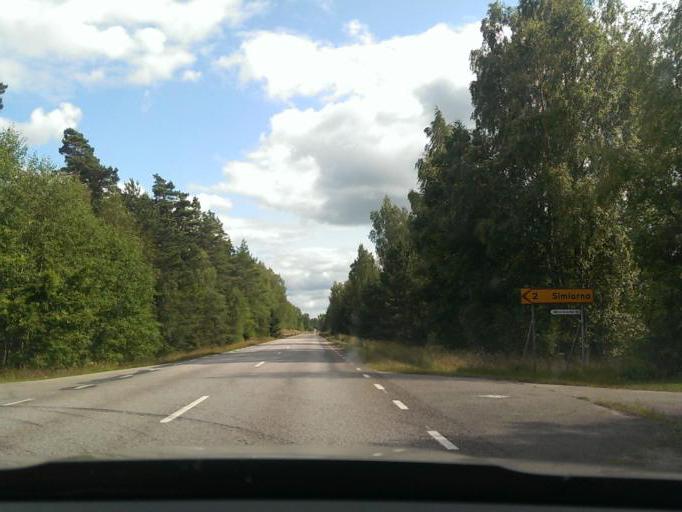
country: SE
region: Kronoberg
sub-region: Ljungby Kommun
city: Lagan
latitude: 56.9272
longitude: 13.9838
